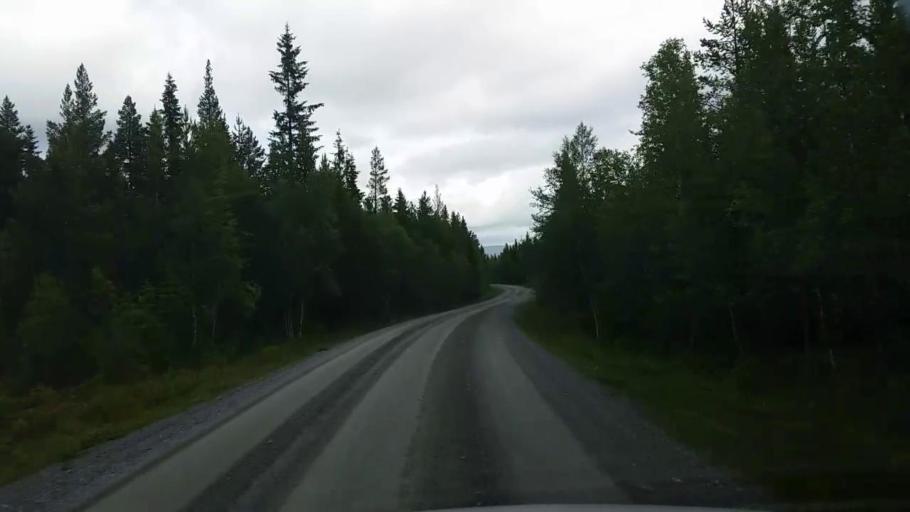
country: NO
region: Hedmark
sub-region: Engerdal
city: Engerdal
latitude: 62.4055
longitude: 12.6650
